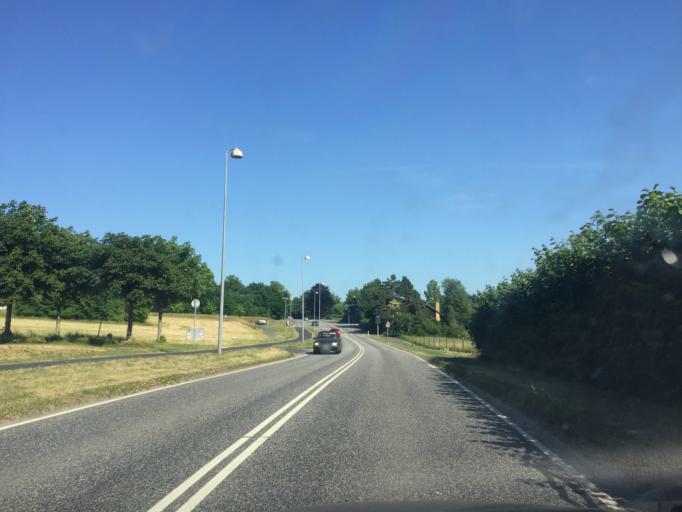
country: DK
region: Capital Region
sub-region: Fureso Kommune
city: Vaerlose
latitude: 55.7826
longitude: 12.3469
